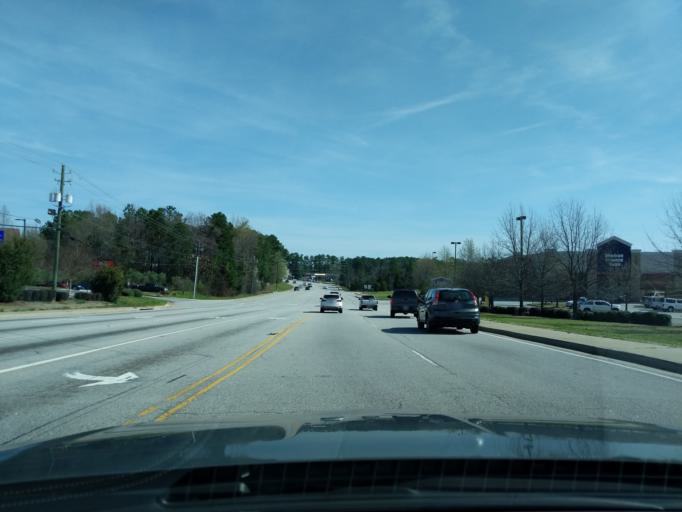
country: US
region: Georgia
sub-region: Columbia County
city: Evans
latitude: 33.5372
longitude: -82.1280
